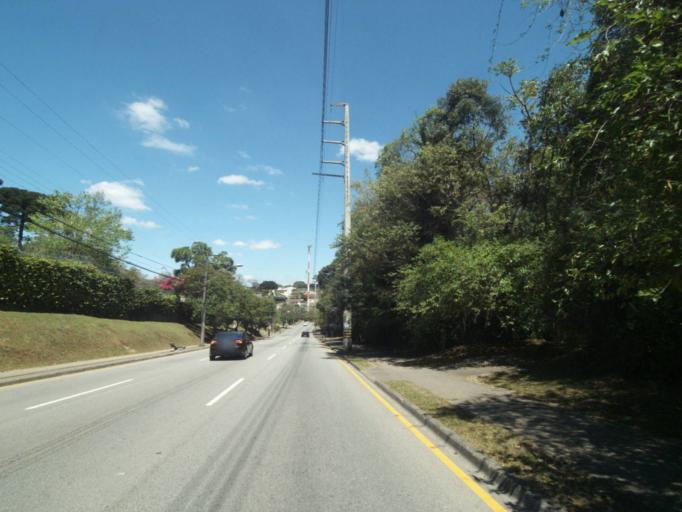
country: BR
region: Parana
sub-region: Curitiba
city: Curitiba
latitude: -25.3967
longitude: -49.2735
